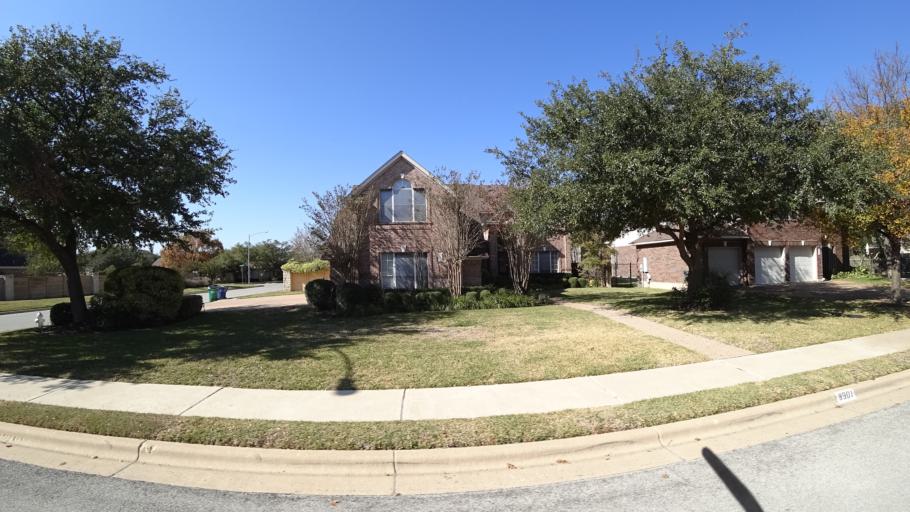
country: US
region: Texas
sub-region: Travis County
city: Lost Creek
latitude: 30.3725
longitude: -97.8451
